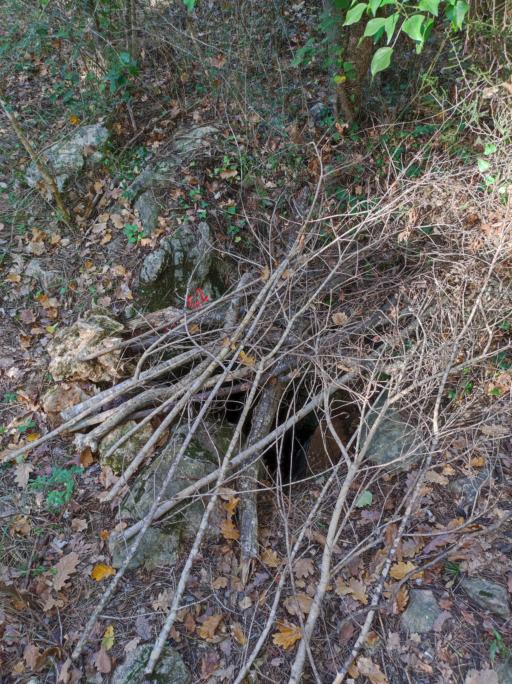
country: FR
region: Provence-Alpes-Cote d'Azur
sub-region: Departement des Alpes-Maritimes
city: Le Rouret
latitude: 43.6742
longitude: 7.0534
